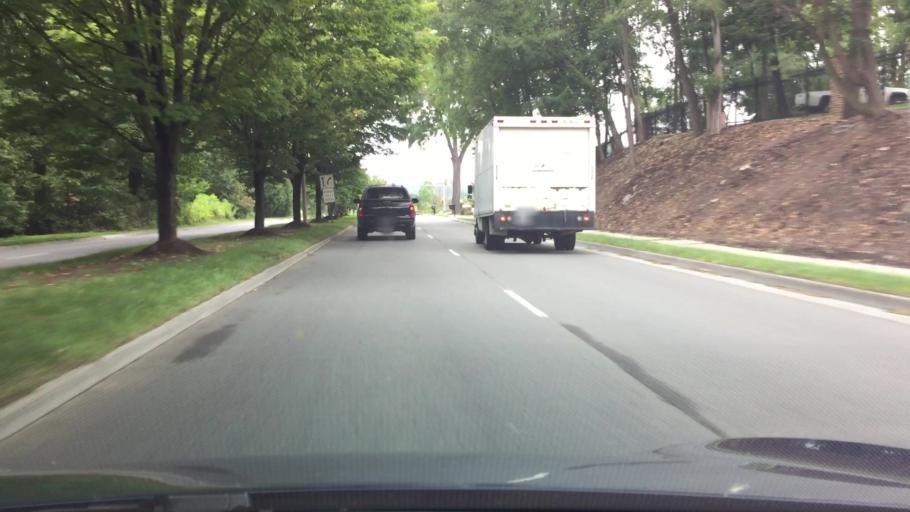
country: US
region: Virginia
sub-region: City of Radford
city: Radford
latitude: 37.1317
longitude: -80.5493
